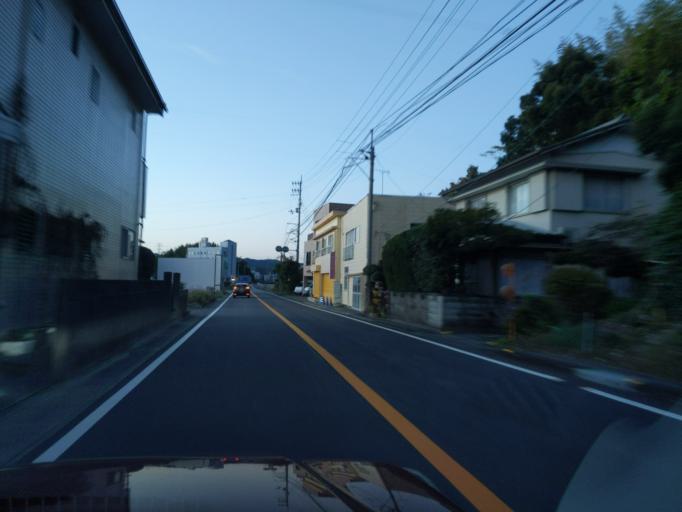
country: JP
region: Tokushima
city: Anan
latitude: 33.8667
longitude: 134.6324
